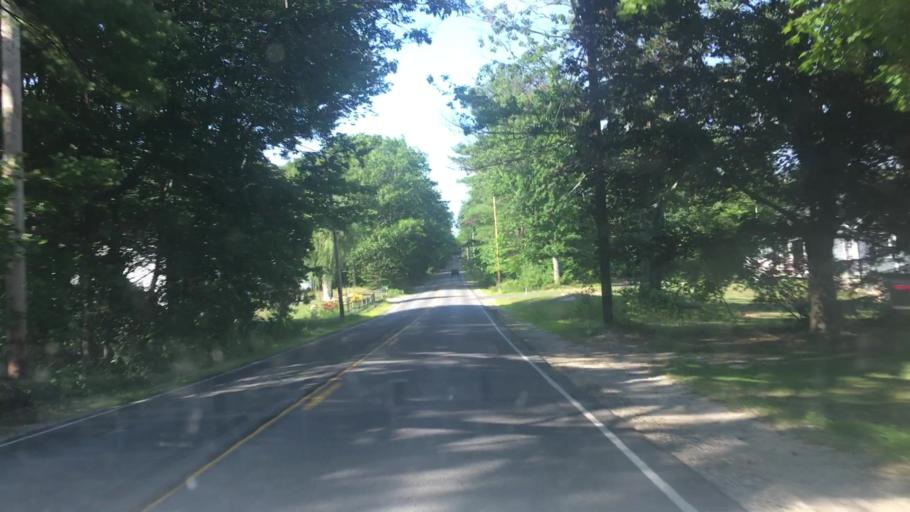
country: US
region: Maine
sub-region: York County
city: Buxton
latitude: 43.7151
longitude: -70.5693
